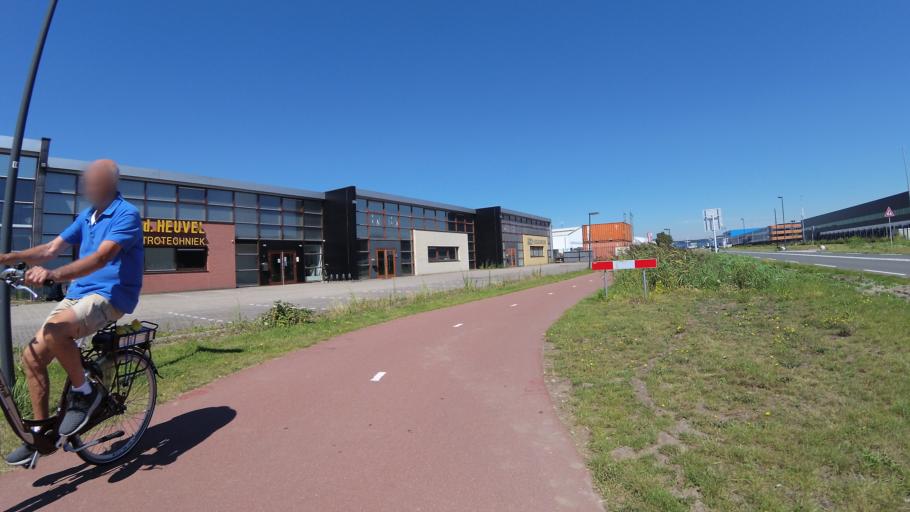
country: NL
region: North Brabant
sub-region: Gemeente Waalwijk
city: Waalwijk
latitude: 51.6954
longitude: 5.0689
